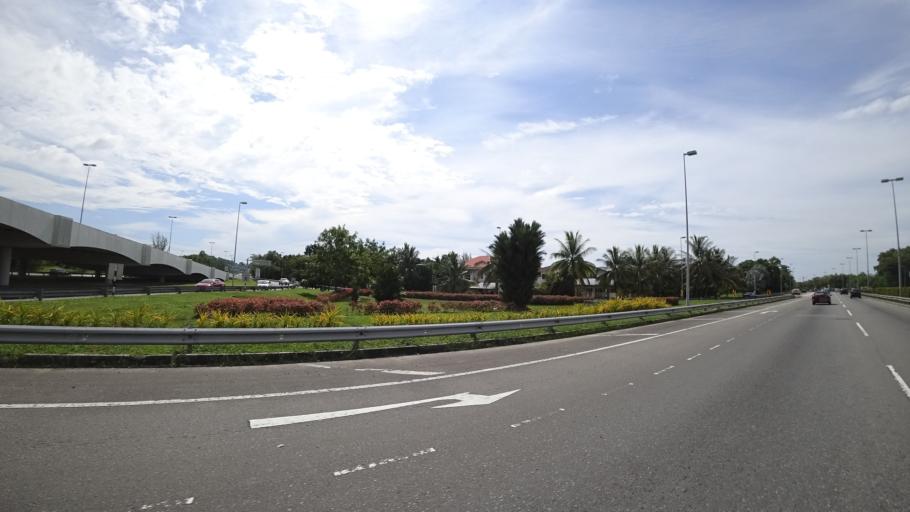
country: BN
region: Brunei and Muara
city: Bandar Seri Begawan
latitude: 4.9154
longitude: 114.9216
